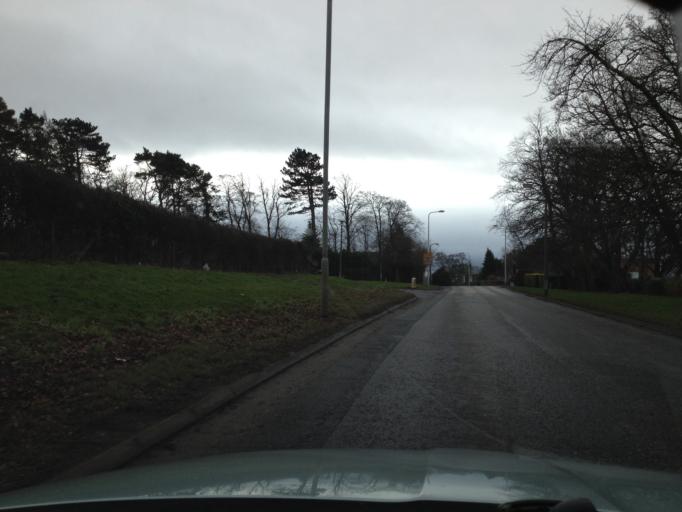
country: GB
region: Scotland
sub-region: Edinburgh
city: Colinton
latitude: 55.9495
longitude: -3.2790
